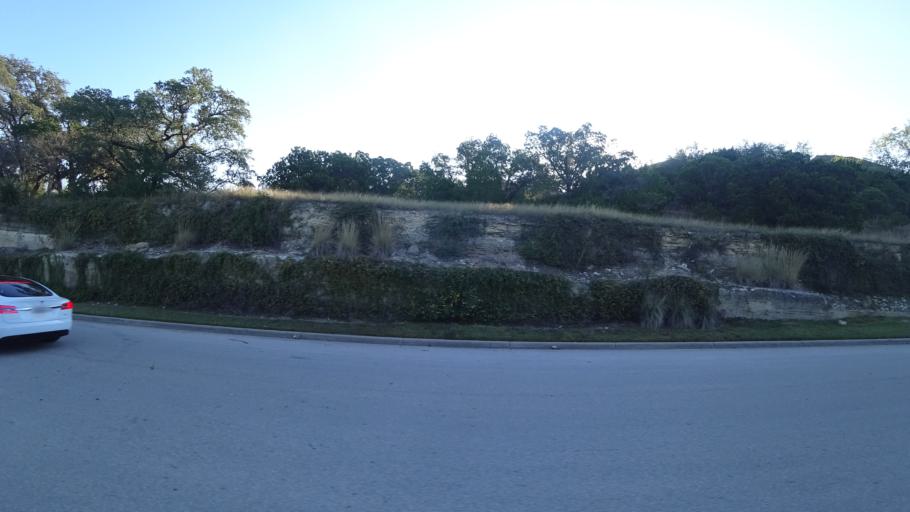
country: US
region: Texas
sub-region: Travis County
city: Hudson Bend
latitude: 30.3772
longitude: -97.8828
